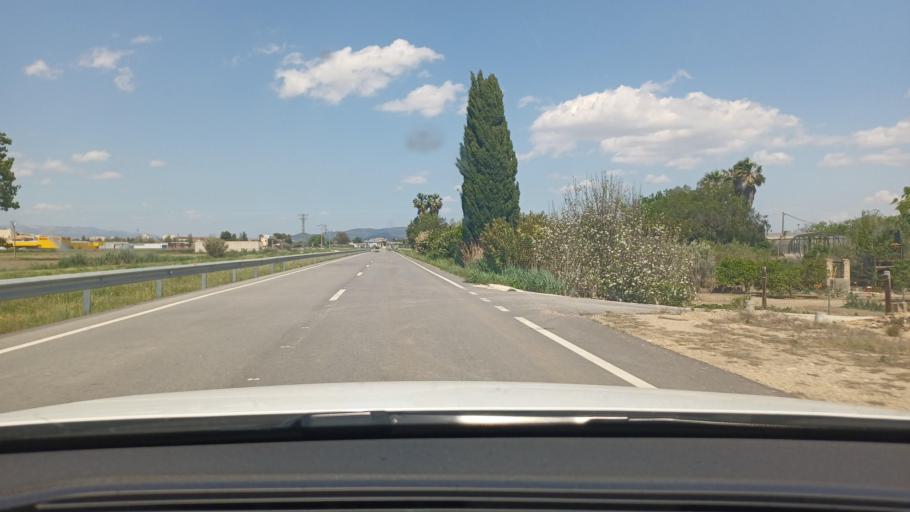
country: ES
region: Catalonia
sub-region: Provincia de Tarragona
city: Amposta
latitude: 40.6976
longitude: 0.5891
